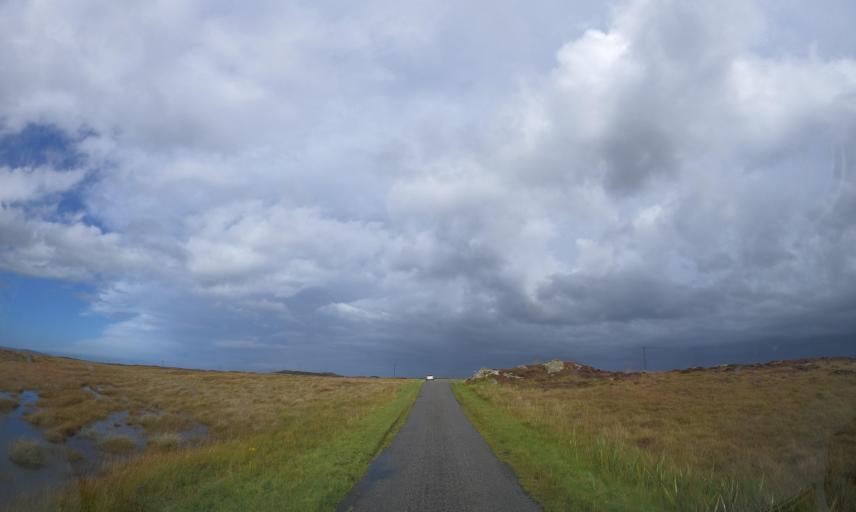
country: GB
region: Scotland
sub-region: Eilean Siar
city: Barra
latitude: 56.5147
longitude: -6.8322
